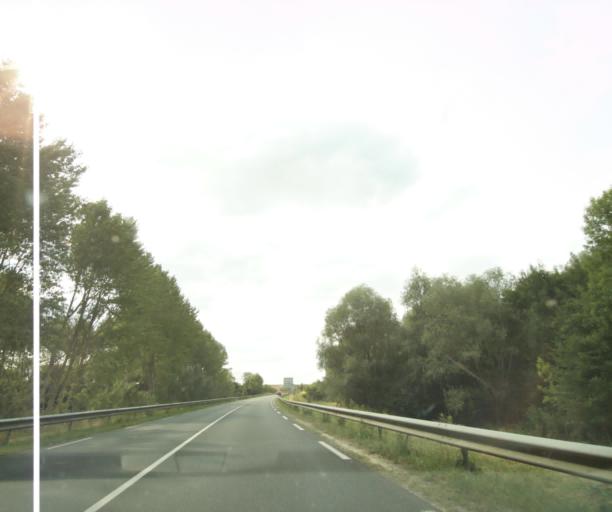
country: FR
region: Centre
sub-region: Departement de l'Indre
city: Buzancais
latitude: 46.8781
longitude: 1.4219
